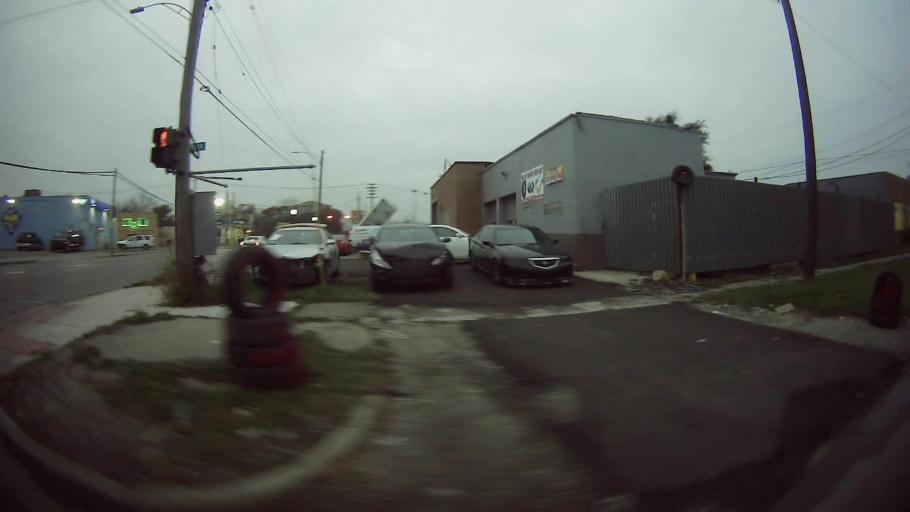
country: US
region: Michigan
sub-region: Wayne County
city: Hamtramck
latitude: 42.4188
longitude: -83.0626
